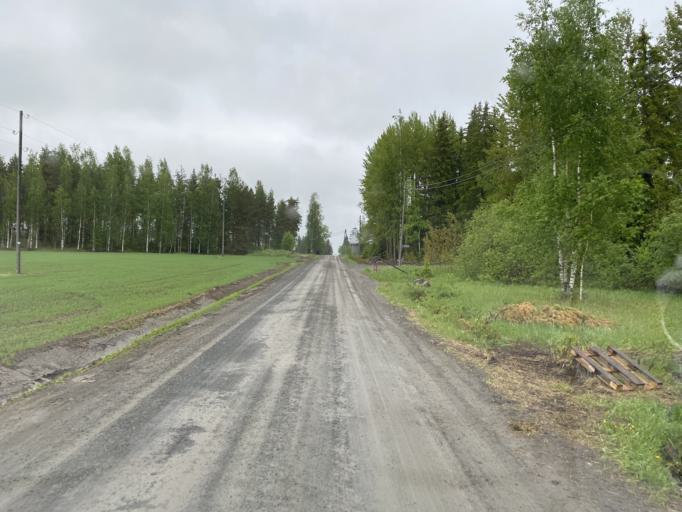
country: FI
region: Haeme
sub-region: Forssa
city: Forssa
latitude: 60.9392
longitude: 23.5865
